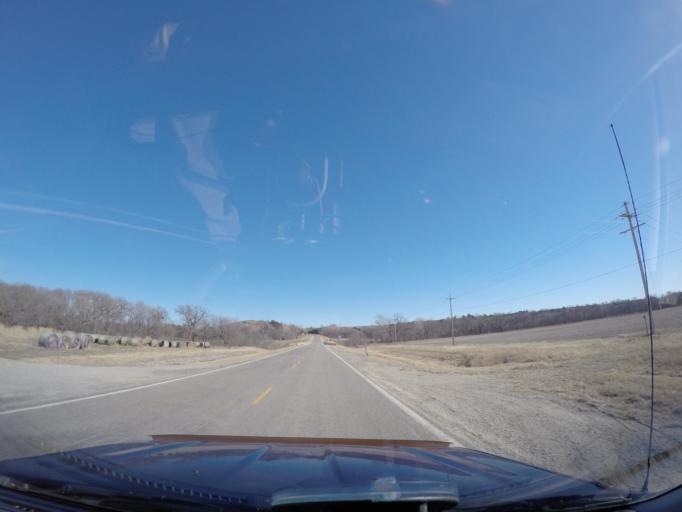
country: US
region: Kansas
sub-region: Dickinson County
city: Herington
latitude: 38.7976
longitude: -96.9422
